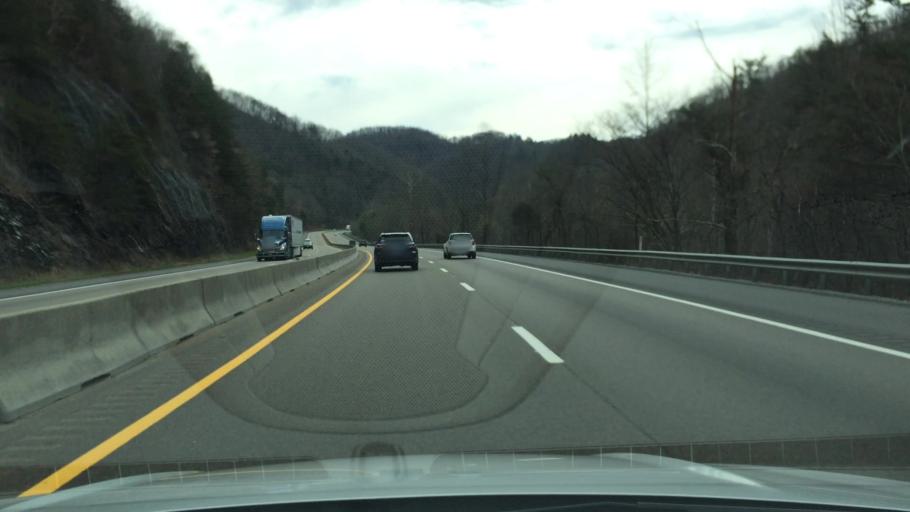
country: US
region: Tennessee
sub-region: Cocke County
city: Newport
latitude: 35.8056
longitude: -83.1372
